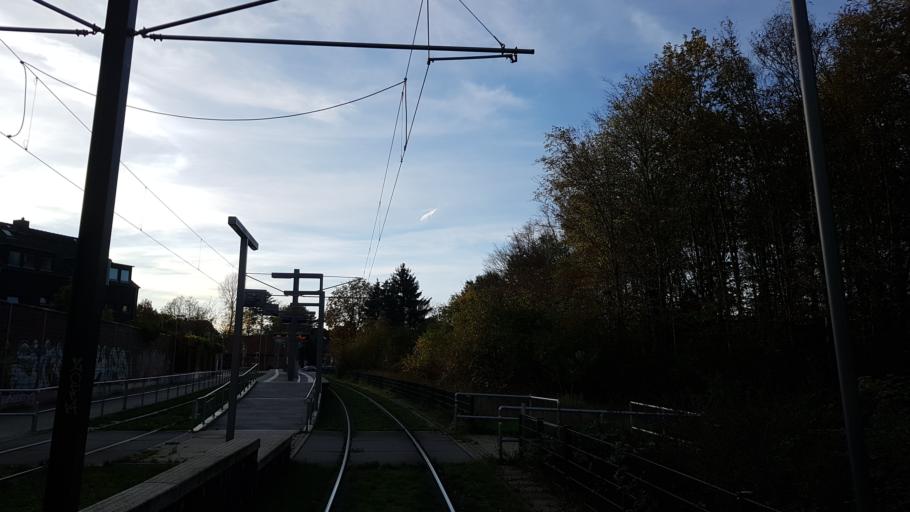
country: DE
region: Lower Saxony
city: Isernhagen Farster Bauerschaft
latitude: 52.3928
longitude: 9.8502
